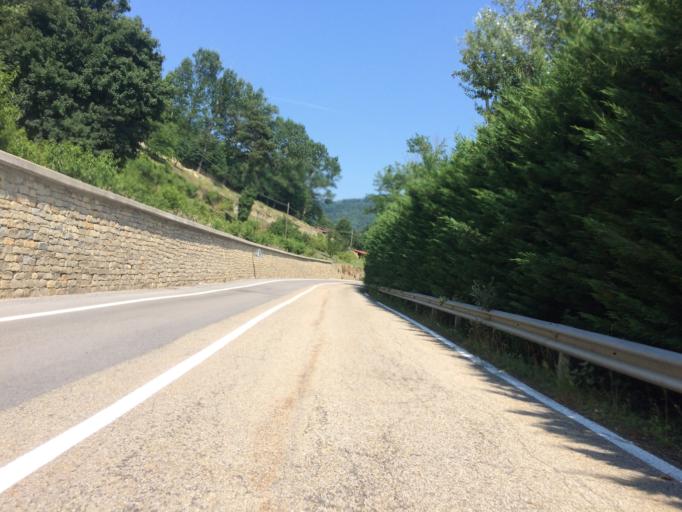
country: IT
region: Piedmont
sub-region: Provincia di Cuneo
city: Torre Bormida
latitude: 44.5598
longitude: 8.1594
